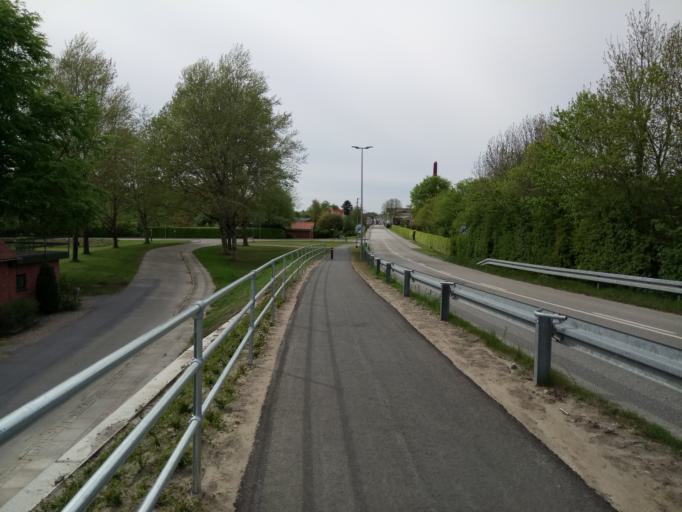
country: DK
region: Central Jutland
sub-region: Ringkobing-Skjern Kommune
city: Tarm
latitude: 55.9038
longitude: 8.5281
